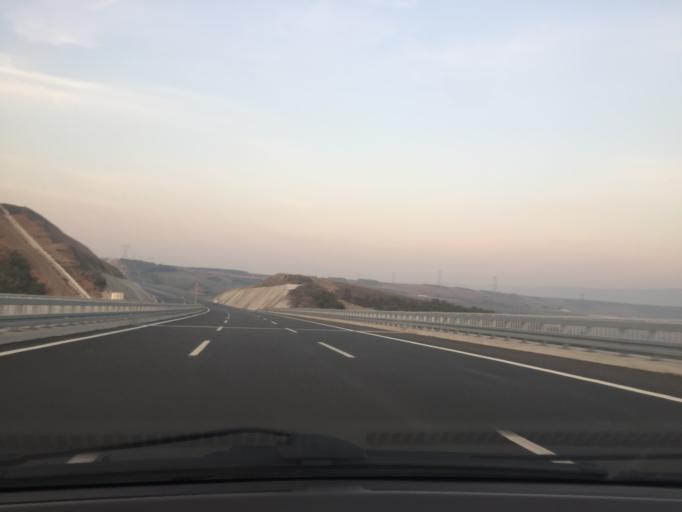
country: TR
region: Bursa
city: Mahmudiye
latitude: 40.2767
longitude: 28.5203
